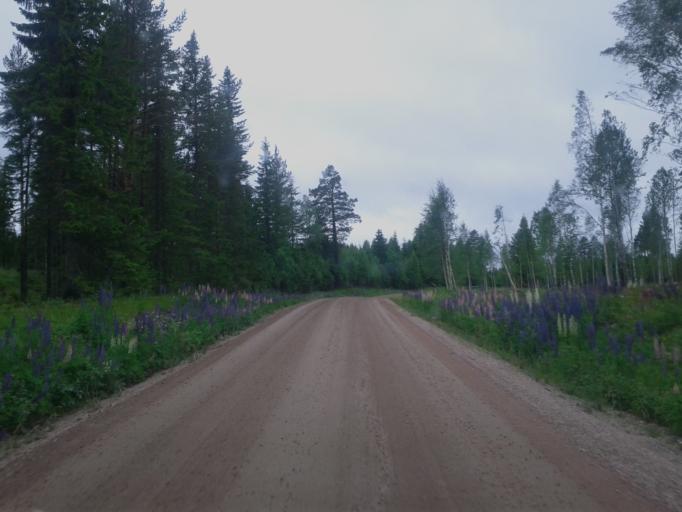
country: SE
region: Gaevleborg
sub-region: Hudiksvalls Kommun
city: Delsbo
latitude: 62.1421
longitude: 16.6130
